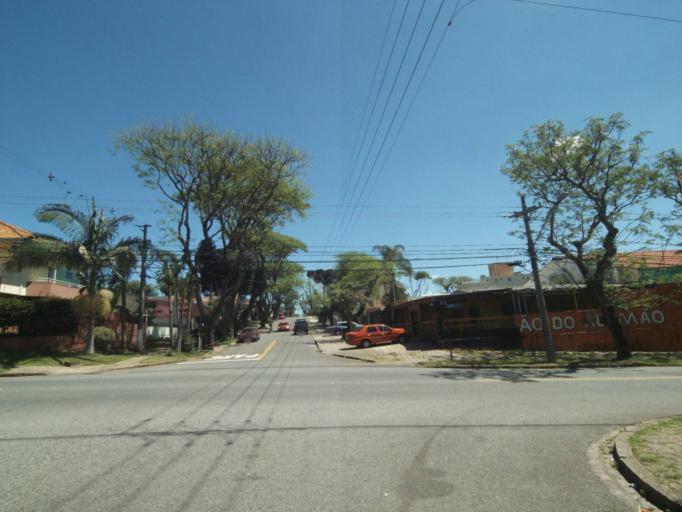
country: BR
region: Parana
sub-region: Curitiba
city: Curitiba
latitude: -25.3899
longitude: -49.2415
